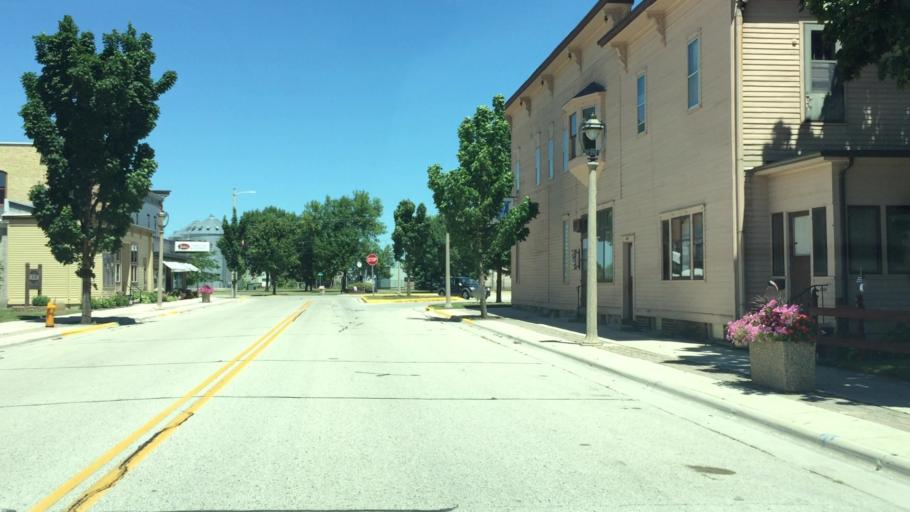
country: US
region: Wisconsin
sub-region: Calumet County
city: New Holstein
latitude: 43.9507
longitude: -88.0864
